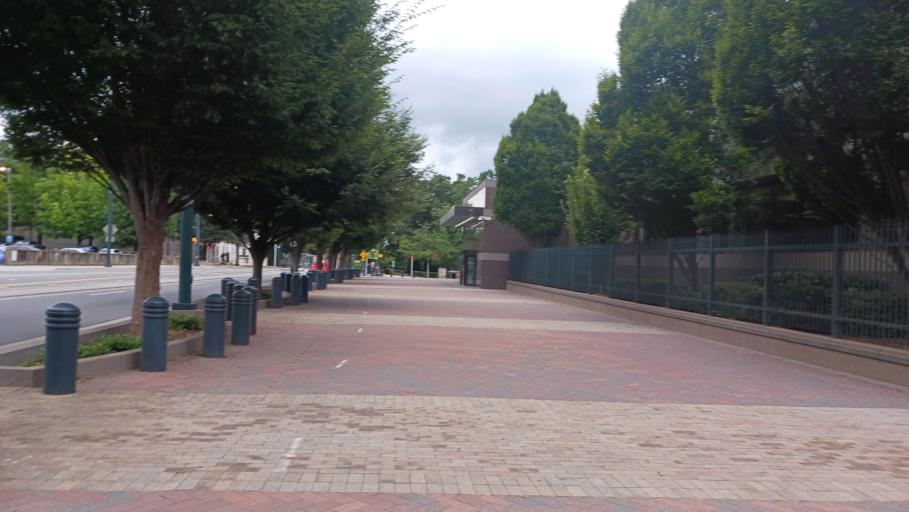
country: US
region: North Carolina
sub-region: Mecklenburg County
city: Charlotte
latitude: 35.2235
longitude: -80.8390
